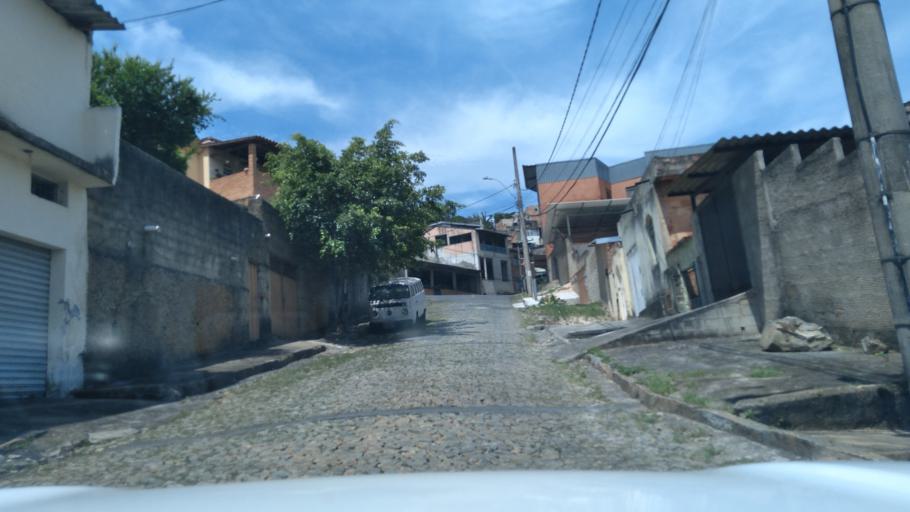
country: BR
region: Minas Gerais
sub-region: Contagem
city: Contagem
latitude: -19.9170
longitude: -44.0234
